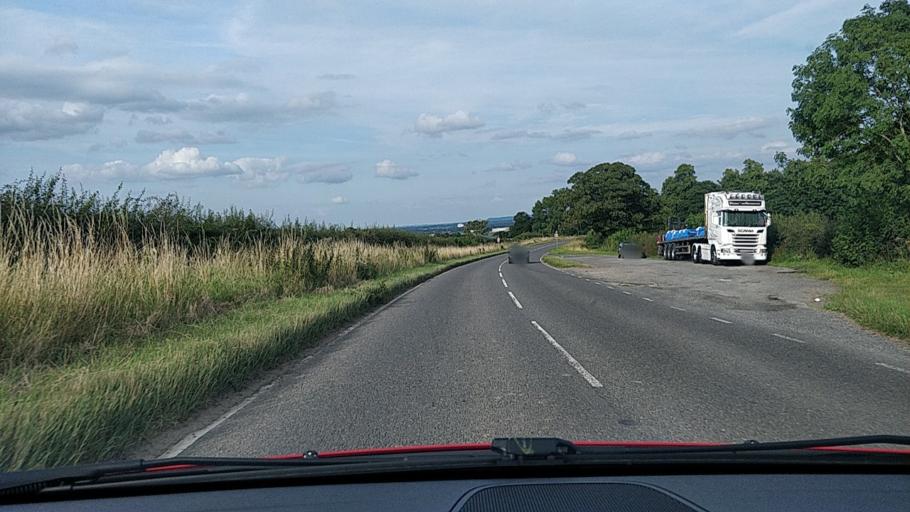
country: GB
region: Wales
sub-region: County of Flintshire
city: Hawarden
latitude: 53.1587
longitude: -3.0182
